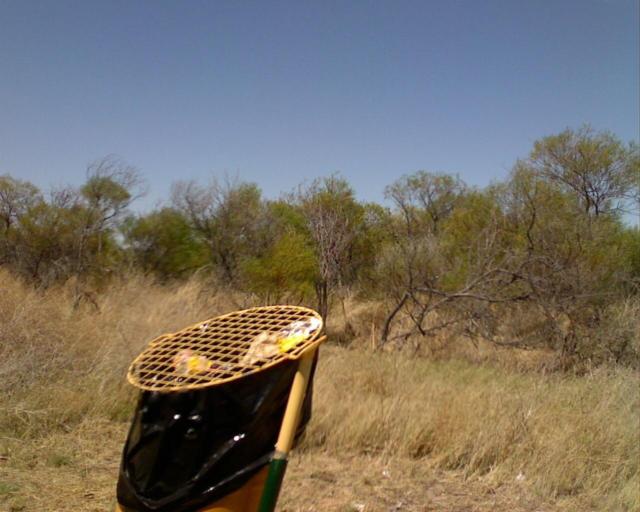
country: AU
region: Western Australia
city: Port Denison
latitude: -29.6603
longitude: 115.2279
